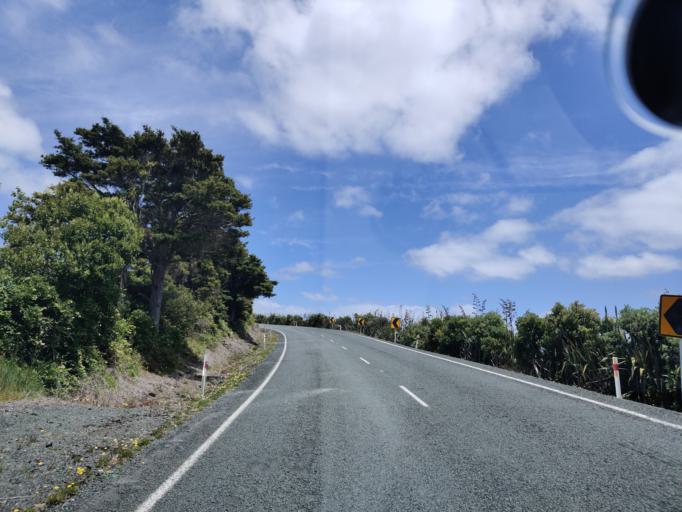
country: NZ
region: Auckland
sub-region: Auckland
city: Wellsford
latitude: -36.3811
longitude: 174.4489
